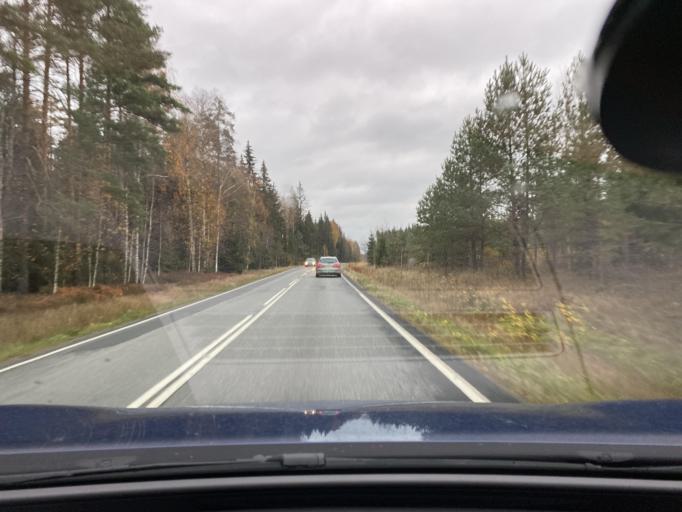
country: FI
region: Satakunta
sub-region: Pori
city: Huittinen
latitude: 61.1204
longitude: 22.5741
